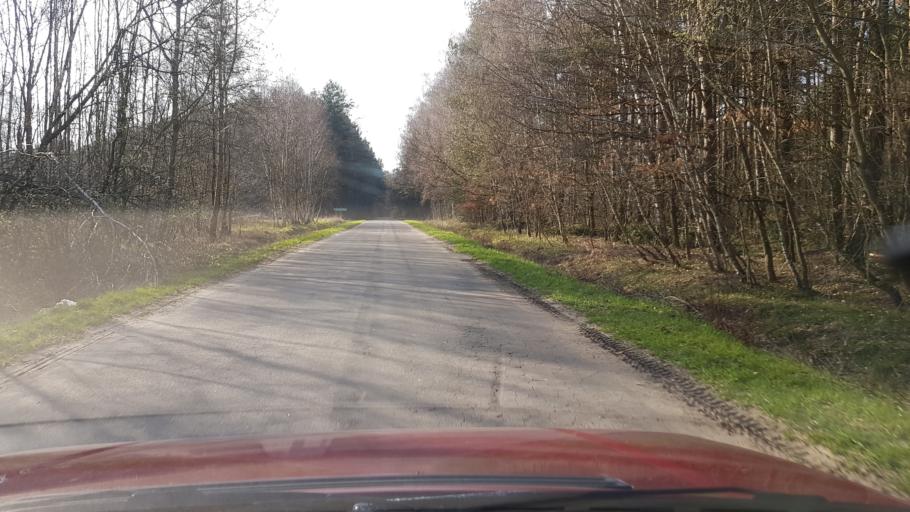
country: PL
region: West Pomeranian Voivodeship
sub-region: Powiat gryficki
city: Ploty
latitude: 53.8302
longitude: 15.3244
